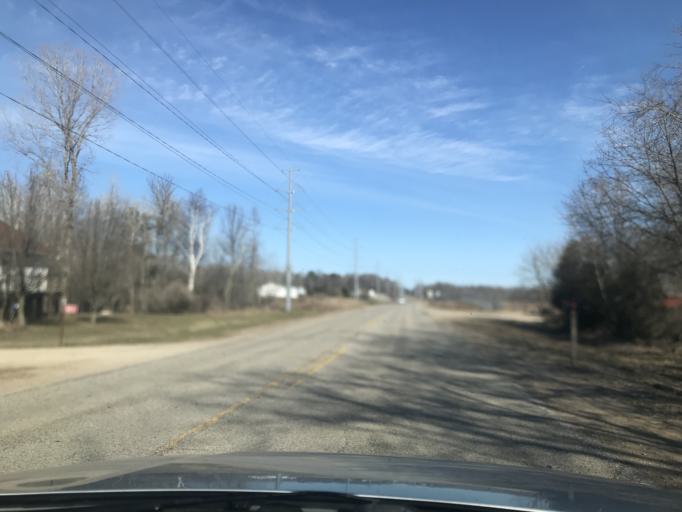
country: US
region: Michigan
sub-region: Menominee County
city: Menominee
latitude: 45.1446
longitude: -87.6343
